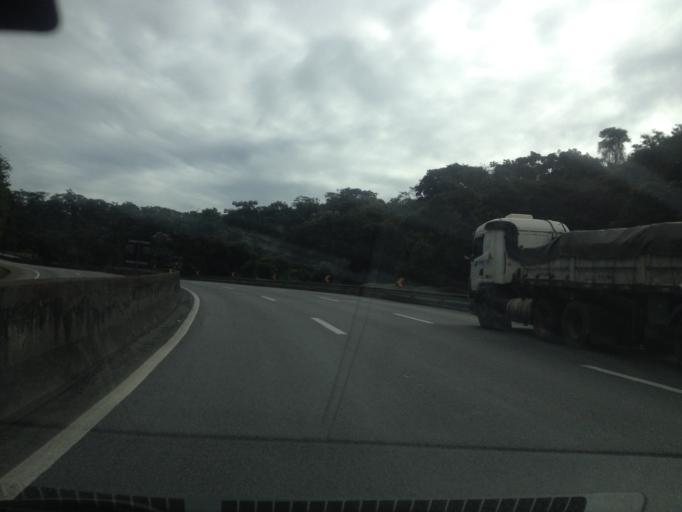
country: BR
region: Rio de Janeiro
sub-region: Pirai
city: Pirai
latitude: -22.6034
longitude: -43.9355
